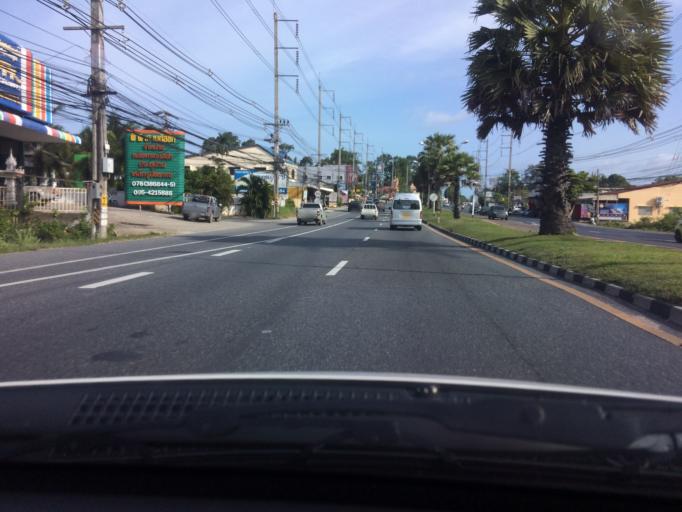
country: TH
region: Phuket
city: Thalang
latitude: 7.9875
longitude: 98.3572
